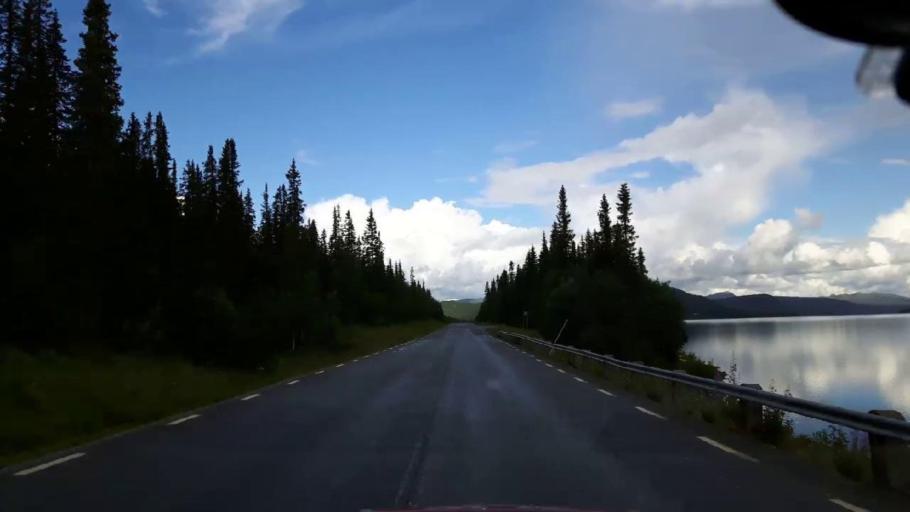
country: SE
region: Vaesterbotten
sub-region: Vilhelmina Kommun
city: Sjoberg
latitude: 65.0029
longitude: 15.1935
